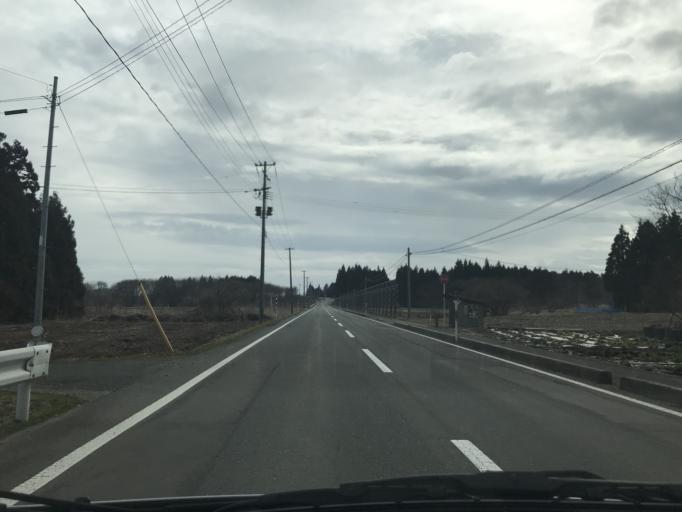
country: JP
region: Iwate
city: Hanamaki
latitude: 39.3811
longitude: 141.0079
